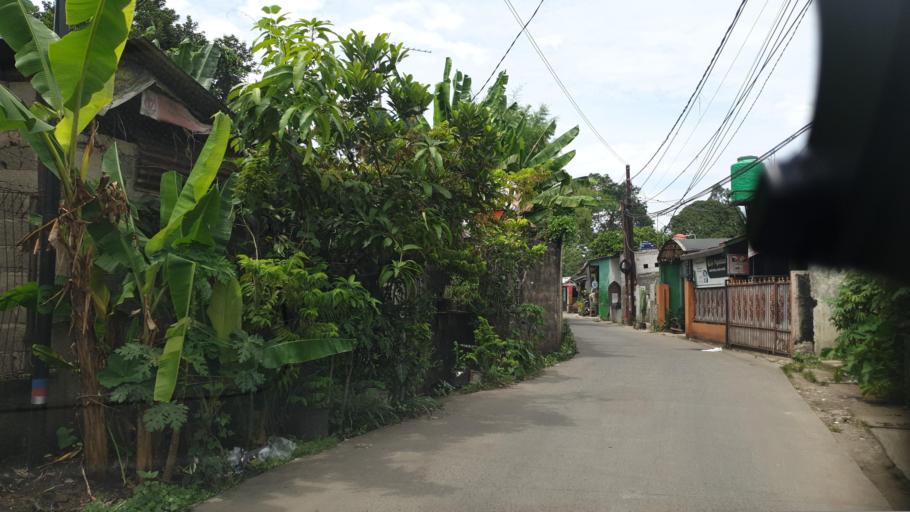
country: ID
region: West Java
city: Pamulang
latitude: -6.3663
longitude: 106.7485
